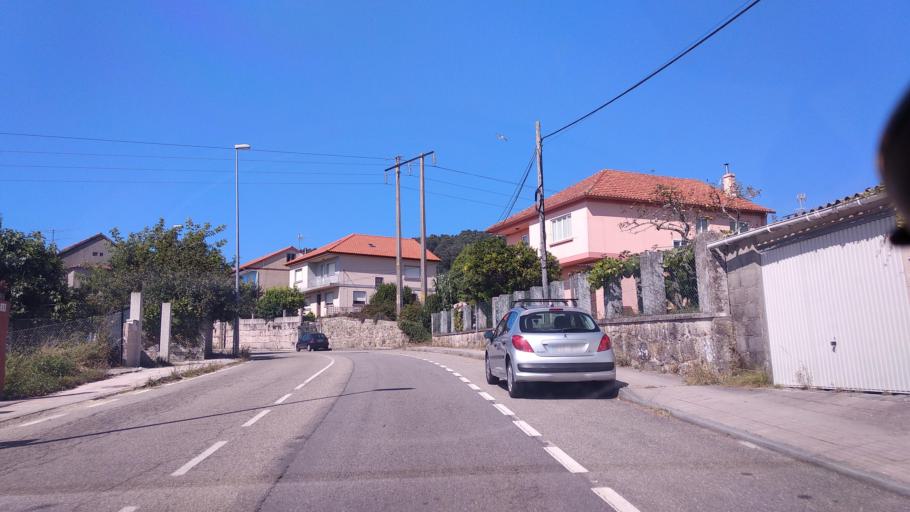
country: ES
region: Galicia
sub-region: Provincia de Pontevedra
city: Moana
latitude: 42.2750
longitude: -8.7674
